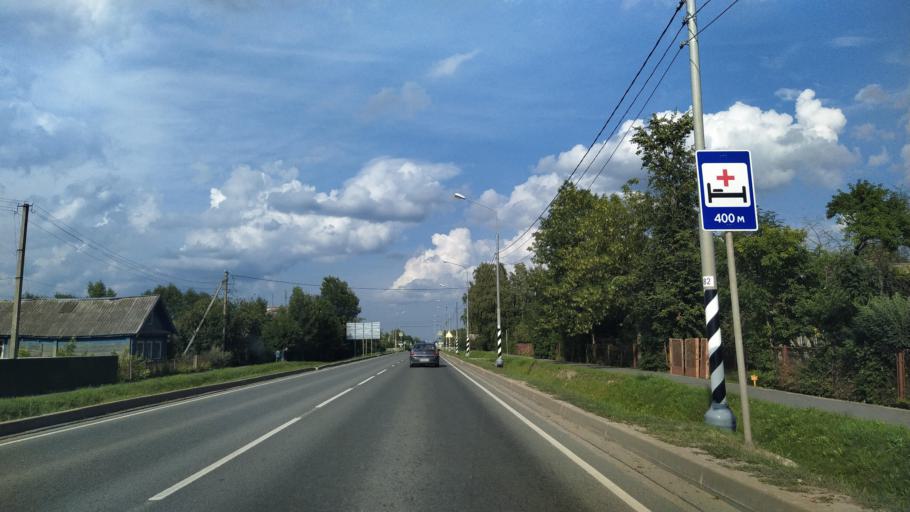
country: RU
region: Novgorod
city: Shimsk
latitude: 58.2105
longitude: 30.7221
